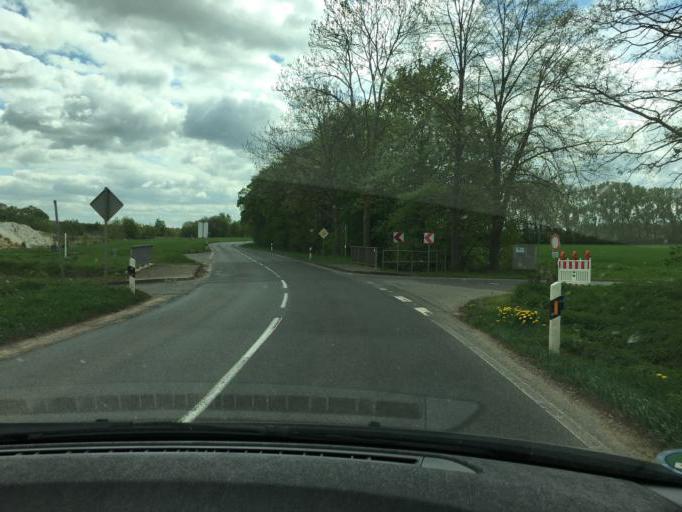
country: DE
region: North Rhine-Westphalia
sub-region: Regierungsbezirk Koln
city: Bad Munstereifel
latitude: 50.6144
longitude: 6.7262
